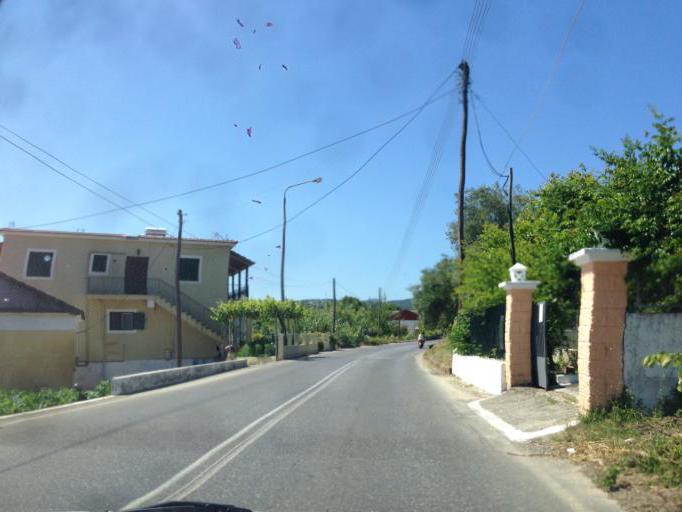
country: GR
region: Ionian Islands
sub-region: Nomos Kerkyras
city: Agios Georgis
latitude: 39.7564
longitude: 19.7189
